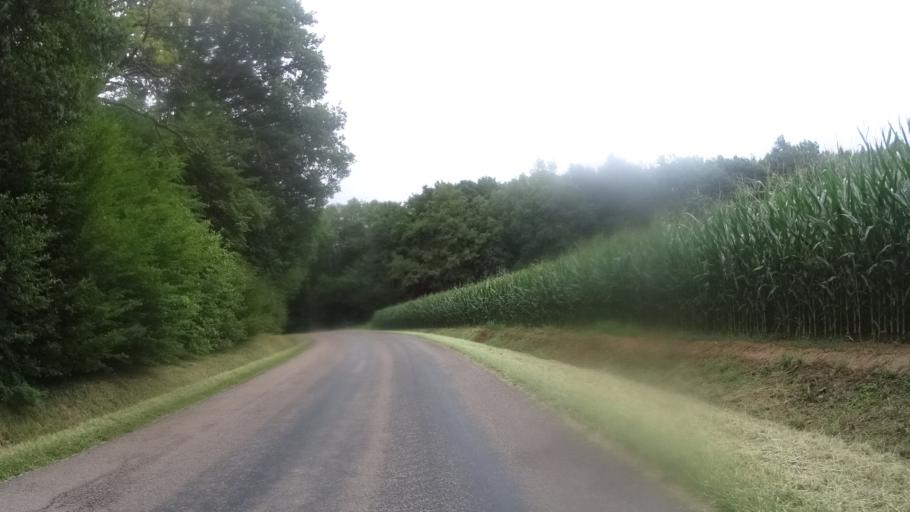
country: FR
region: Champagne-Ardenne
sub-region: Departement de l'Aube
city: Brienne-le-Chateau
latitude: 48.3910
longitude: 4.6463
